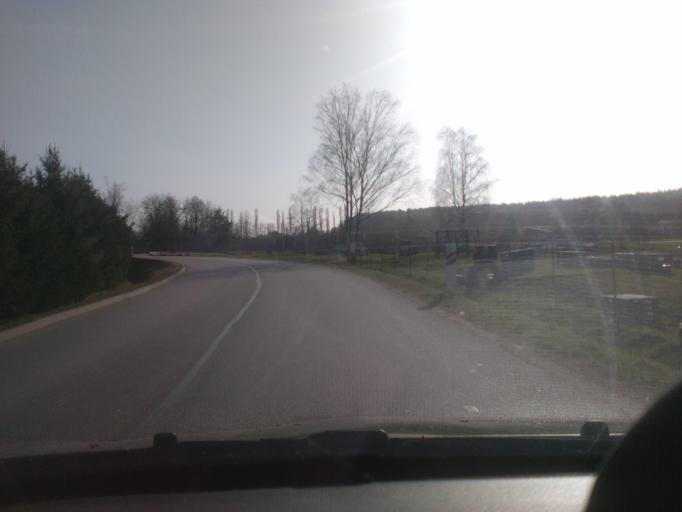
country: FR
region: Lorraine
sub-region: Departement des Vosges
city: Sainte-Marguerite
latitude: 48.2663
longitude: 6.9655
